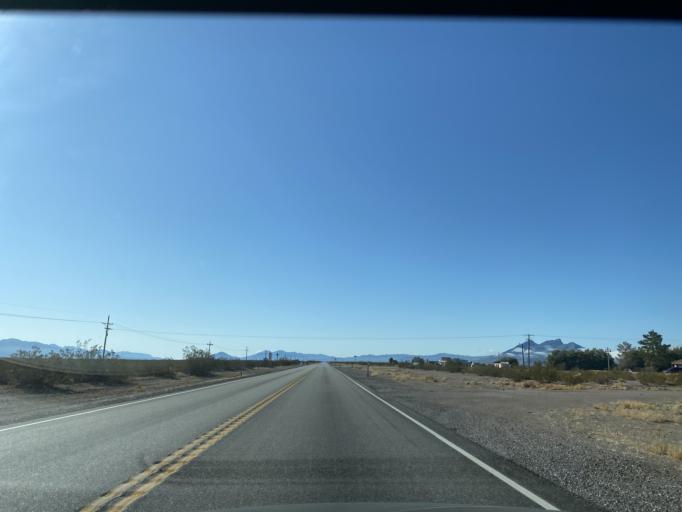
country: US
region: Nevada
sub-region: Nye County
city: Pahrump
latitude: 36.4966
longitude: -116.4214
